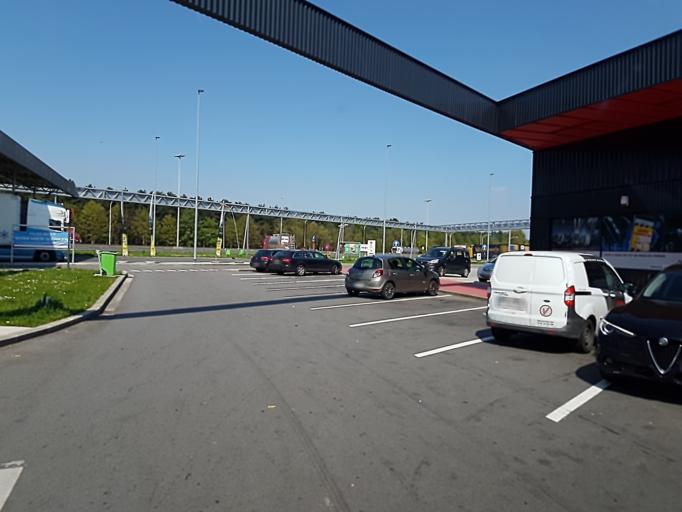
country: BE
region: Flanders
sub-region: Provincie Oost-Vlaanderen
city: Nazareth
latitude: 50.9697
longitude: 3.6073
